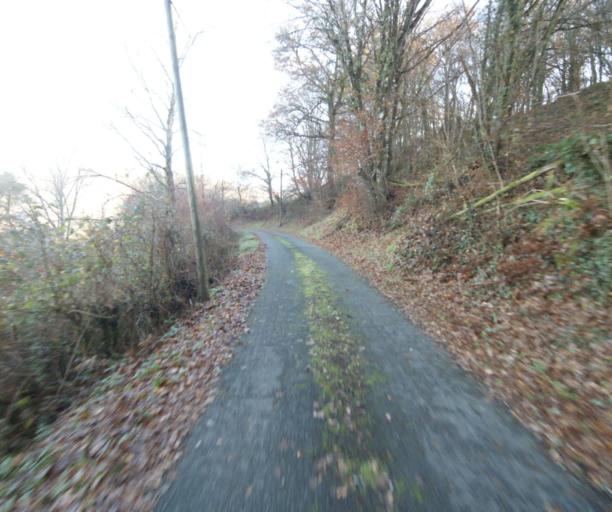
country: FR
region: Limousin
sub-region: Departement de la Correze
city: Laguenne
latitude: 45.2463
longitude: 1.7863
